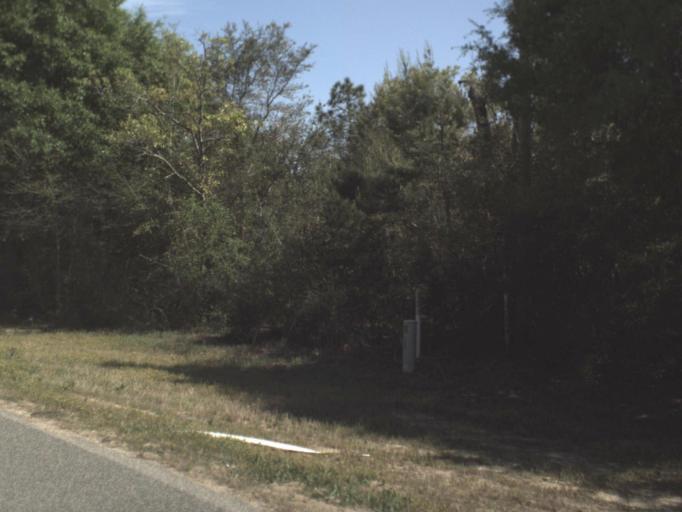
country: US
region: Florida
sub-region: Okaloosa County
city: Crestview
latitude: 30.7524
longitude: -86.4904
